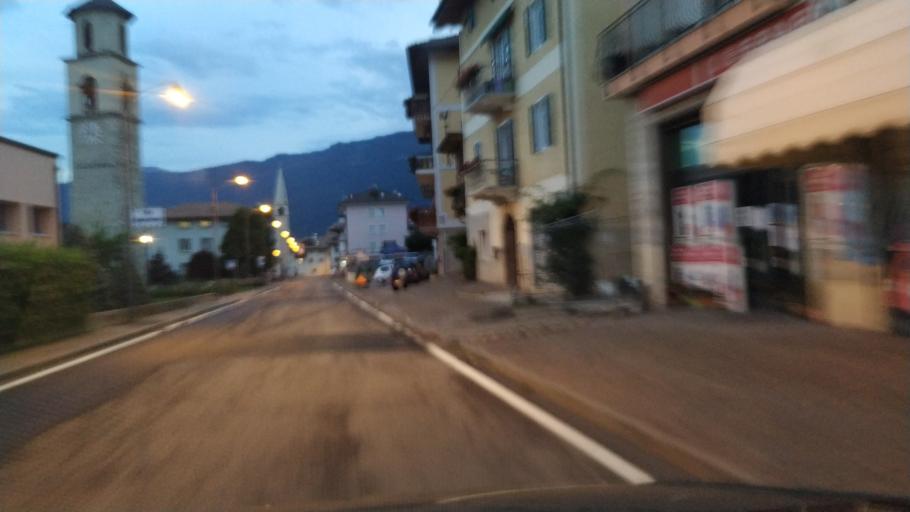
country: IT
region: Trentino-Alto Adige
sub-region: Provincia di Trento
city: Revo
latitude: 46.3917
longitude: 11.0611
